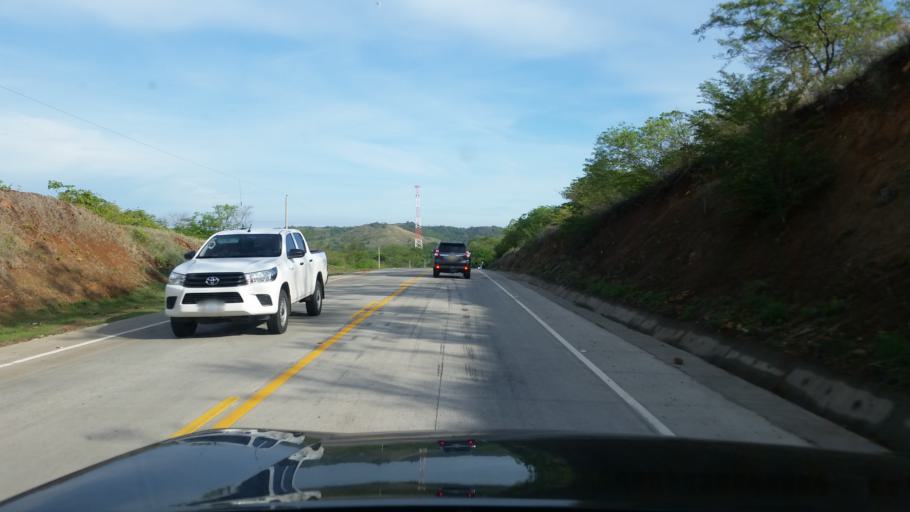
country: NI
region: Leon
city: Nagarote
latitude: 12.1292
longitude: -86.6394
